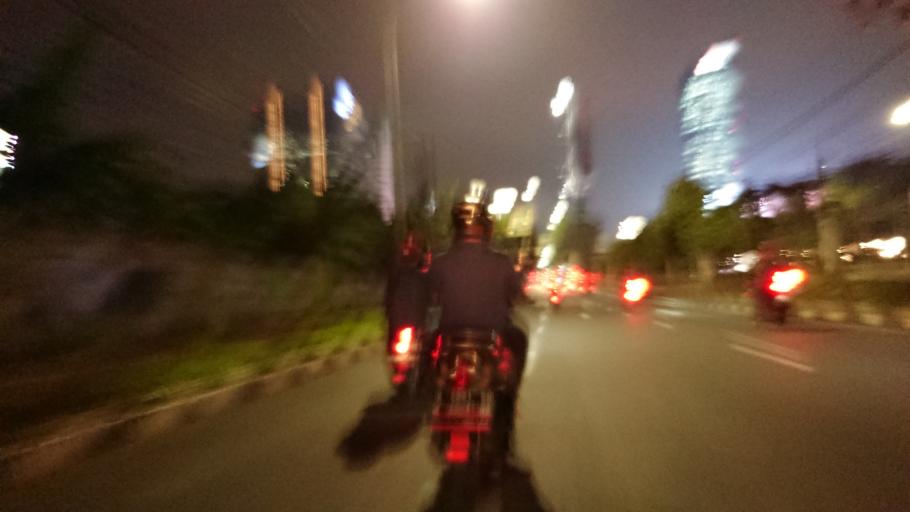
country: ID
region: Jakarta Raya
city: Jakarta
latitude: -6.2045
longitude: 106.7994
